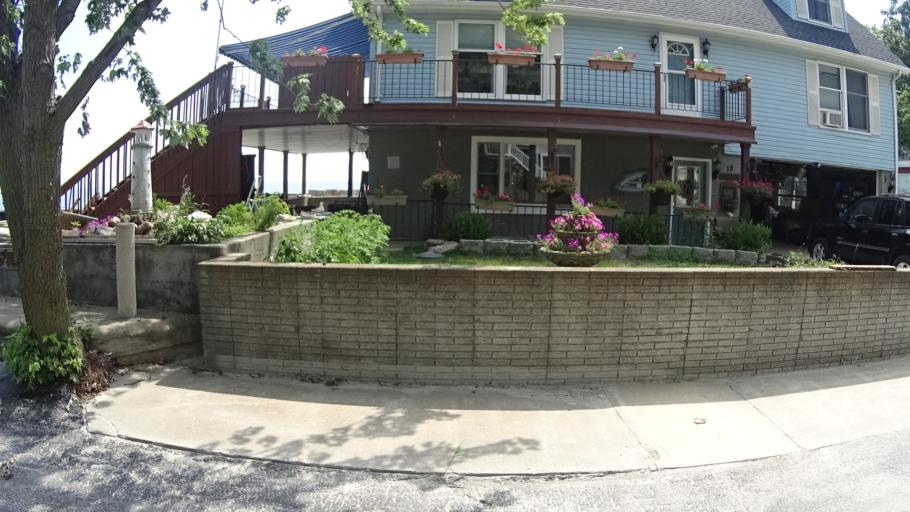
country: US
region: Ohio
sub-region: Erie County
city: Huron
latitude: 41.4112
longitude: -82.5844
